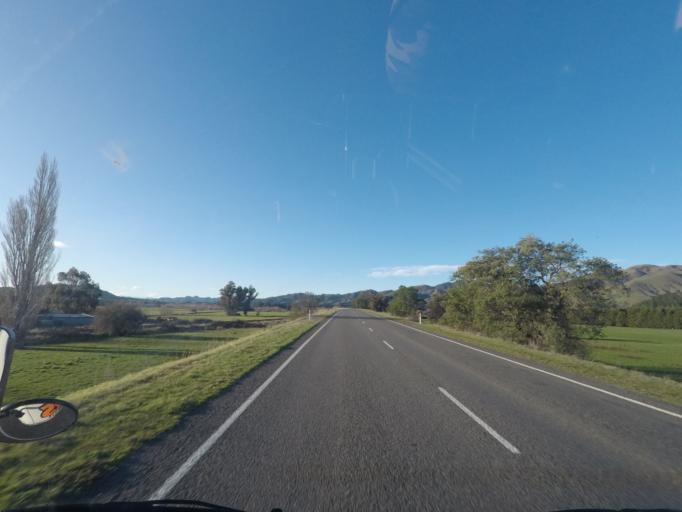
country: NZ
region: Canterbury
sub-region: Kaikoura District
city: Kaikoura
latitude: -42.7073
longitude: 173.2963
